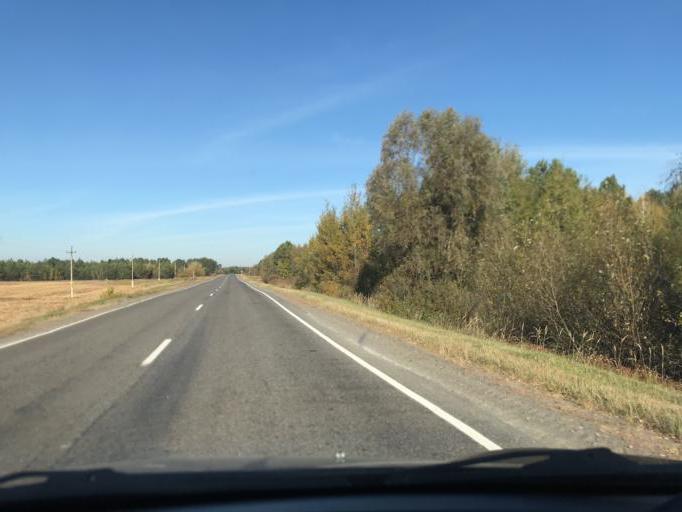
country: UA
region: Chernihiv
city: Lyubech
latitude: 51.5782
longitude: 30.4861
